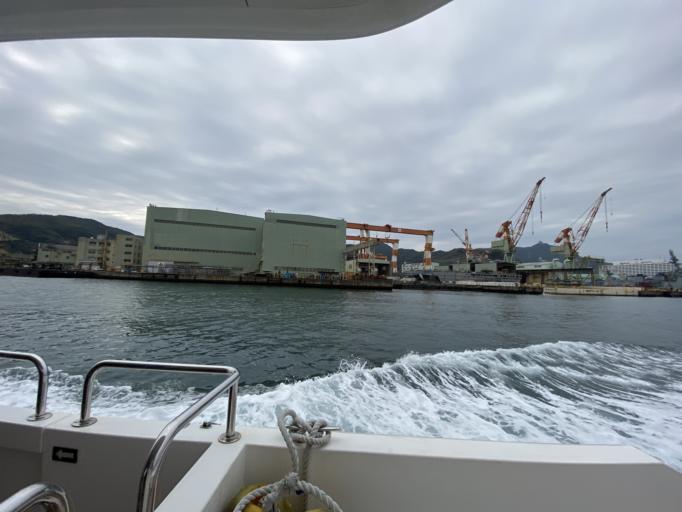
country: JP
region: Nagasaki
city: Nagasaki-shi
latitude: 32.7308
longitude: 129.8574
